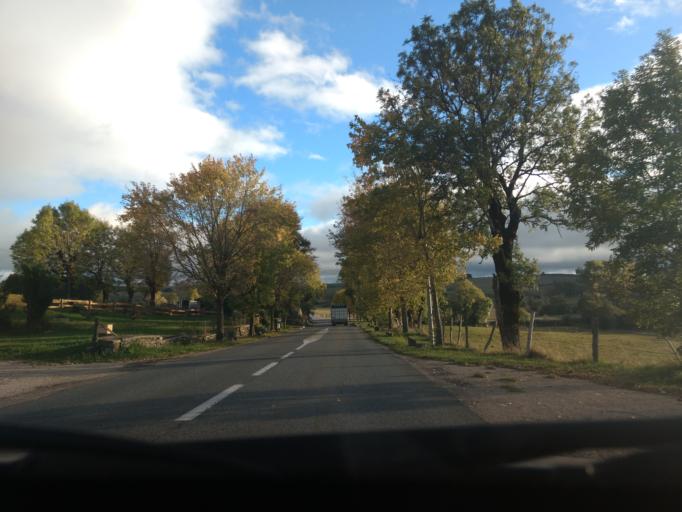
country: FR
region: Midi-Pyrenees
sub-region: Departement de l'Aveyron
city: Laguiole
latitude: 44.7668
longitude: 2.8828
